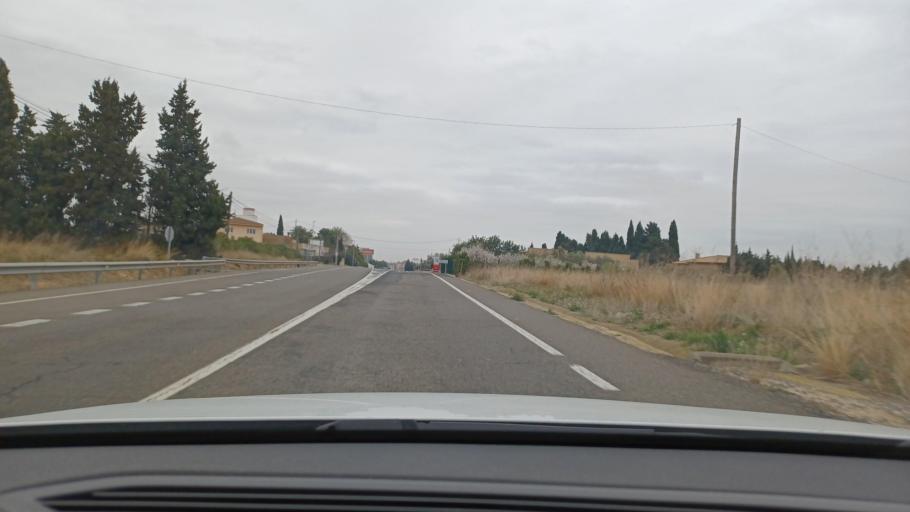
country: ES
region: Catalonia
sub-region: Provincia de Tarragona
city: Amposta
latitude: 40.7510
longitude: 0.6121
